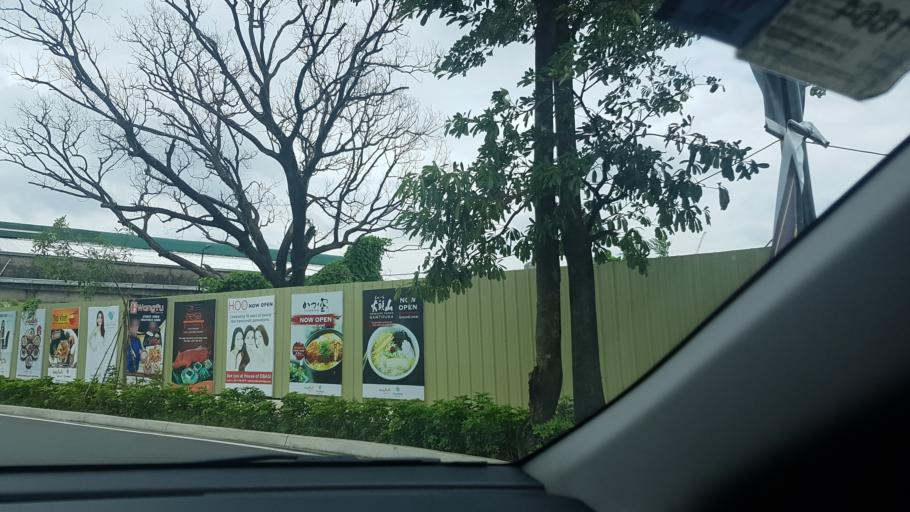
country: PH
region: Calabarzon
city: Del Monte
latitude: 14.6560
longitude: 121.0045
